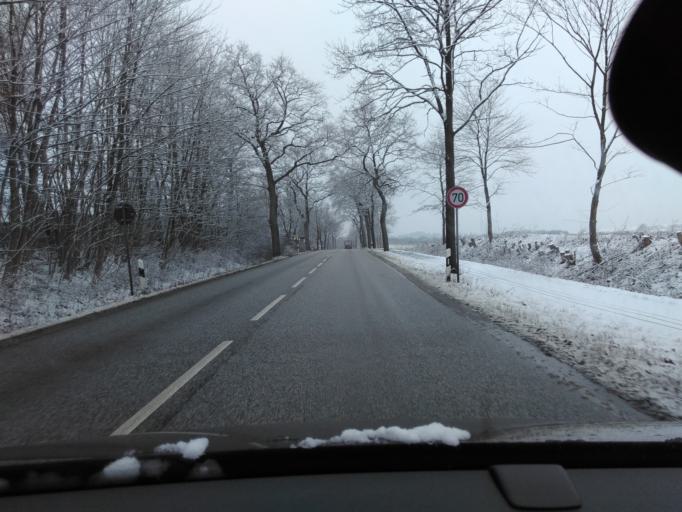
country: DE
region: Schleswig-Holstein
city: Ahrensbok
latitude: 54.0263
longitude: 10.5932
